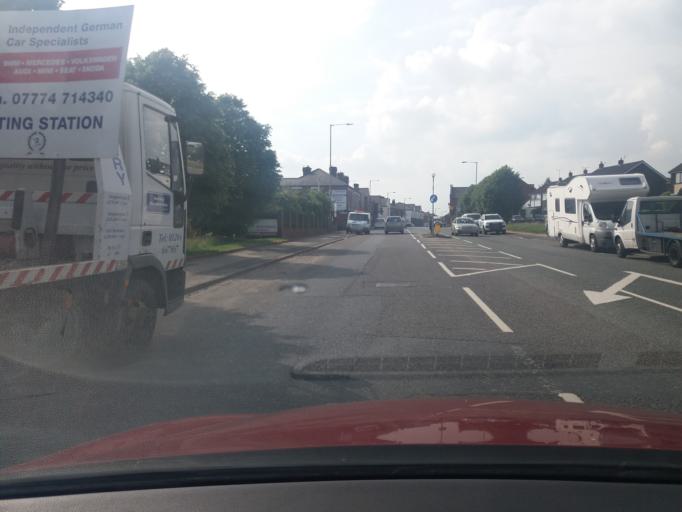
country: GB
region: England
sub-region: Borough of Bolton
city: Horwich
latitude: 53.5917
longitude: -2.5400
